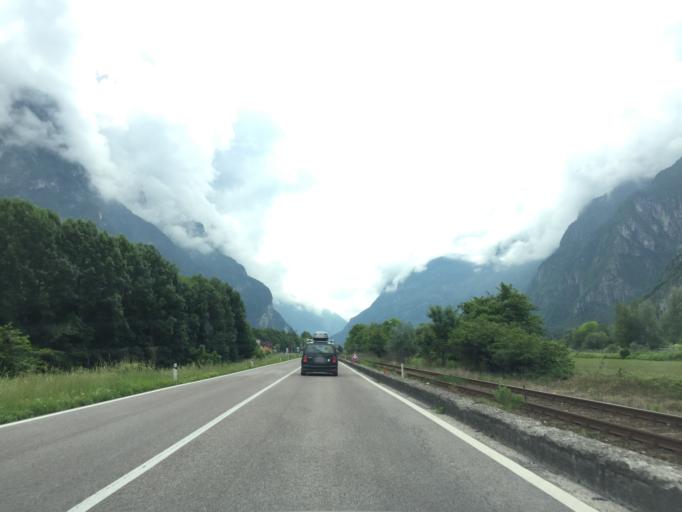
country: IT
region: Trentino-Alto Adige
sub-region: Provincia di Trento
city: Ospedaletto
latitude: 46.0397
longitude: 11.5514
